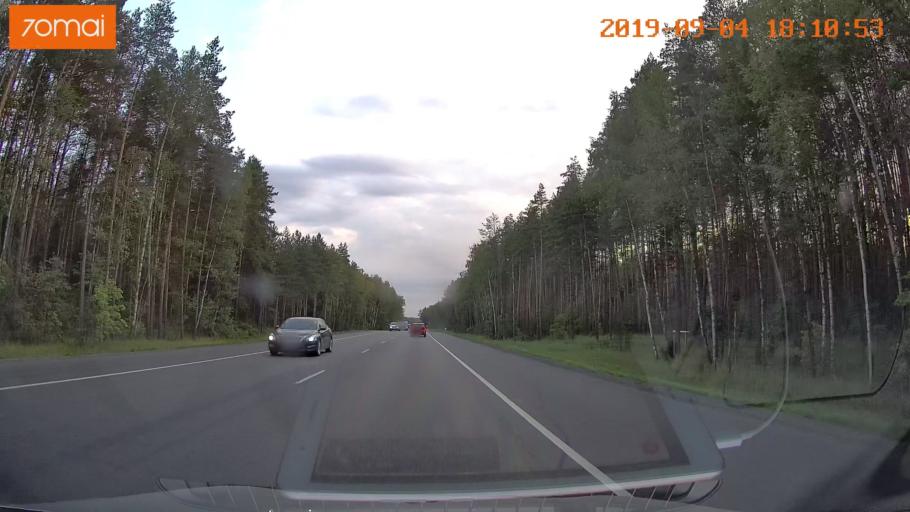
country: RU
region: Moskovskaya
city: Lopatinskiy
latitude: 55.3833
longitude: 38.7603
